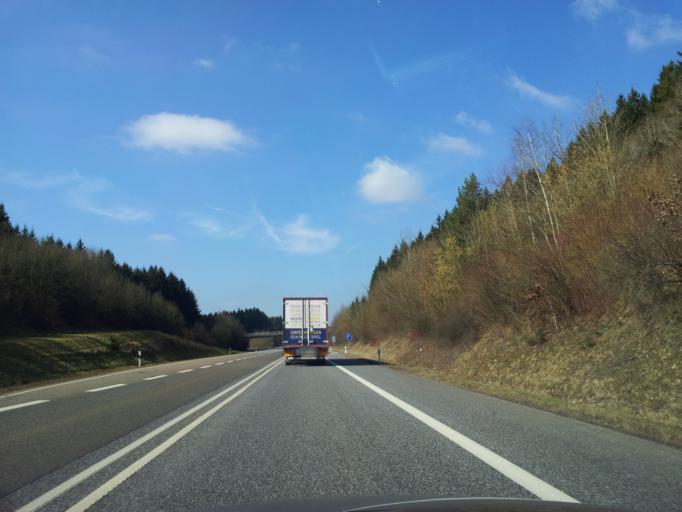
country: DE
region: Rheinland-Pfalz
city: Pittenbach
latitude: 50.2025
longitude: 6.3441
